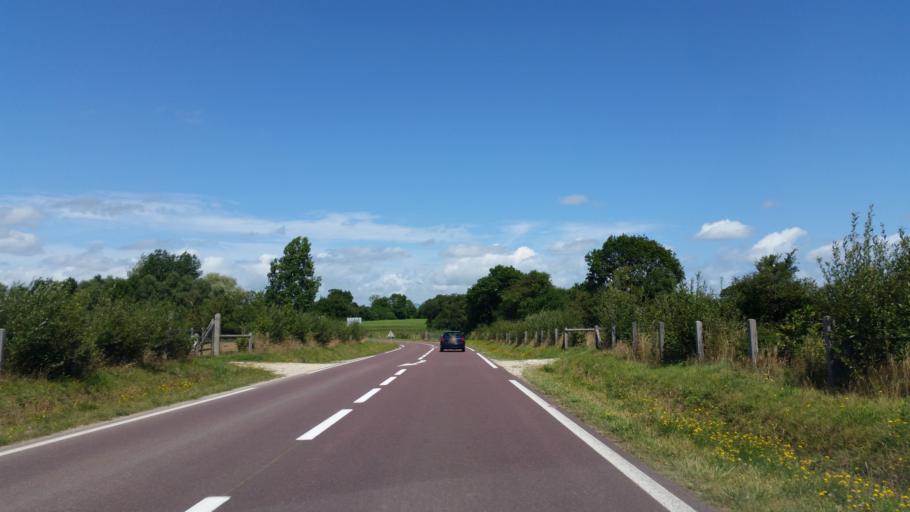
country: FR
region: Lower Normandy
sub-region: Departement de la Manche
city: Sainte-Mere-Eglise
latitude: 49.4037
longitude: -1.3103
